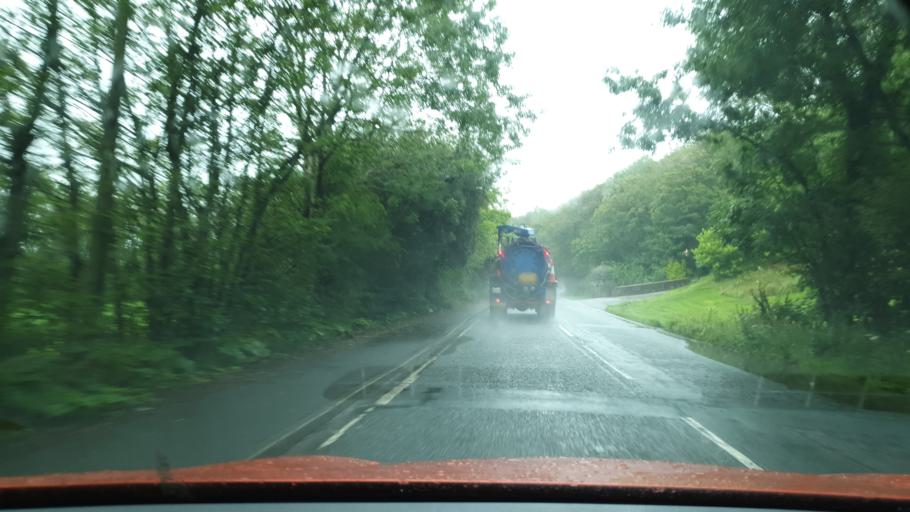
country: GB
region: England
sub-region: Cumbria
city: Millom
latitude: 54.2667
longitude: -3.2156
